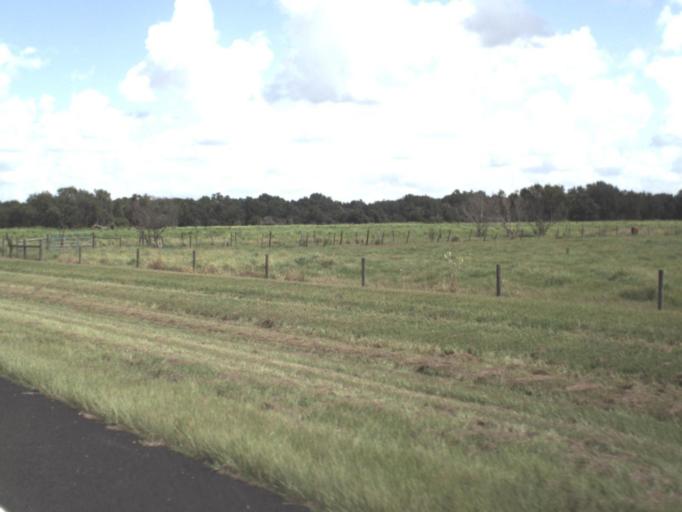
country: US
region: Florida
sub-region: Hardee County
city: Zolfo Springs
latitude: 27.4429
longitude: -81.7964
